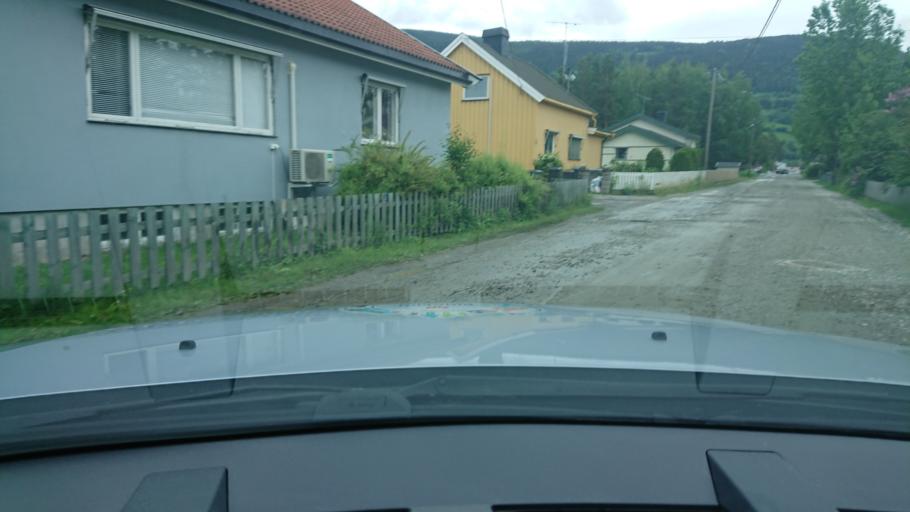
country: NO
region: Oppland
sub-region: Ringebu
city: Ringebu
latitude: 61.5291
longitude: 10.1319
